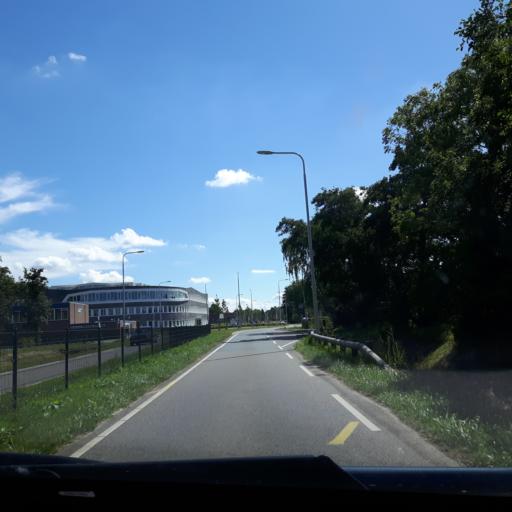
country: NL
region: Zeeland
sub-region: Gemeente Goes
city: Goes
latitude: 51.5019
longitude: 3.9061
